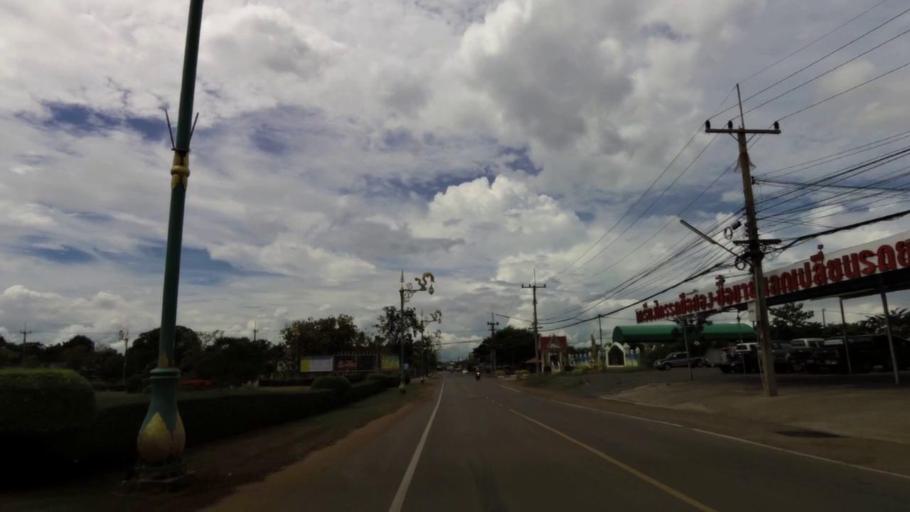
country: TH
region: Nakhon Sawan
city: Phai Sali
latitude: 15.5996
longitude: 100.6571
